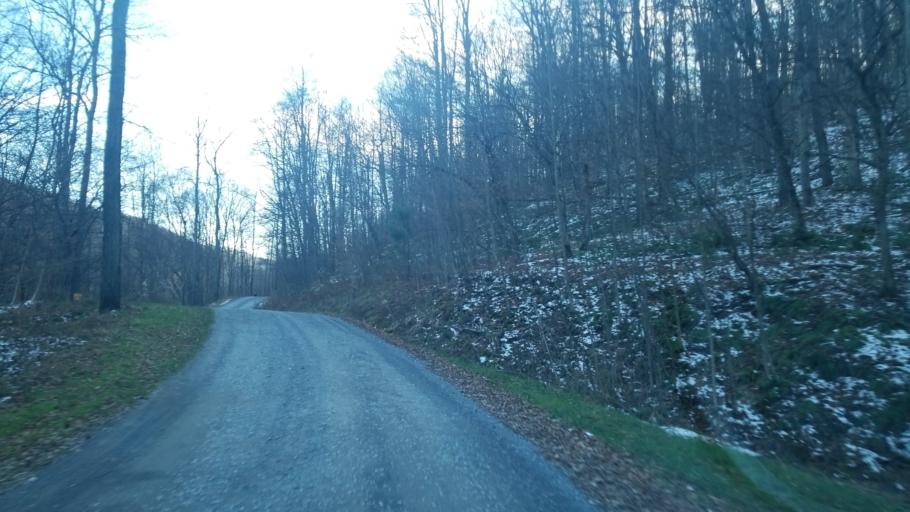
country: US
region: Pennsylvania
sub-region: Potter County
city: Coudersport
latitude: 41.6547
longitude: -78.0866
